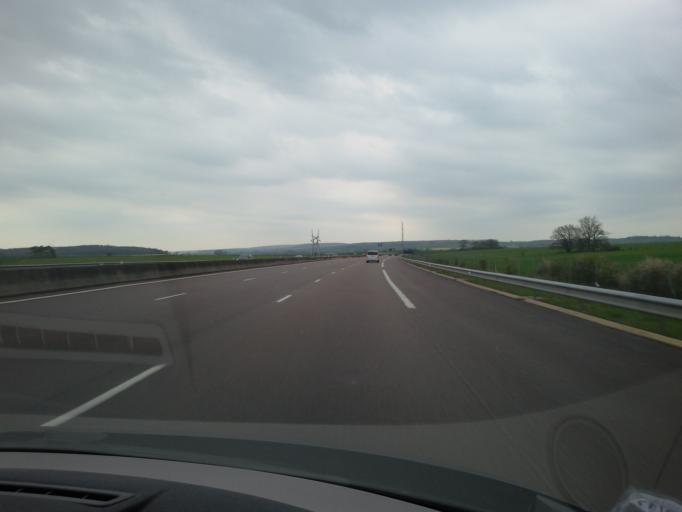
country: FR
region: Champagne-Ardenne
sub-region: Departement de la Haute-Marne
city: Rolampont
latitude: 47.8784
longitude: 5.2203
